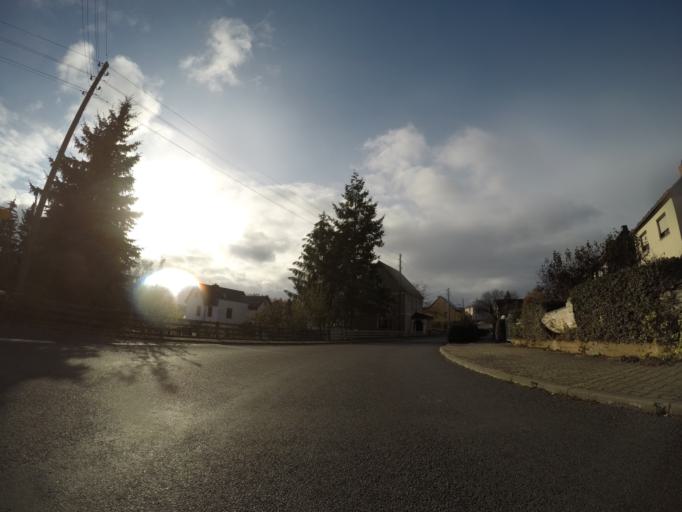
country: DE
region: Thuringia
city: Gossnitz
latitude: 50.8939
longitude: 12.4032
